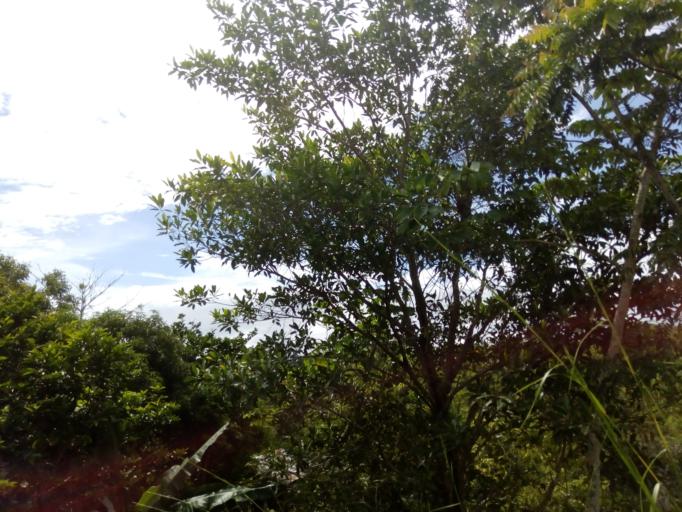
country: CO
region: Boyaca
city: Puerto Boyaca
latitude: 6.0025
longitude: -74.3738
